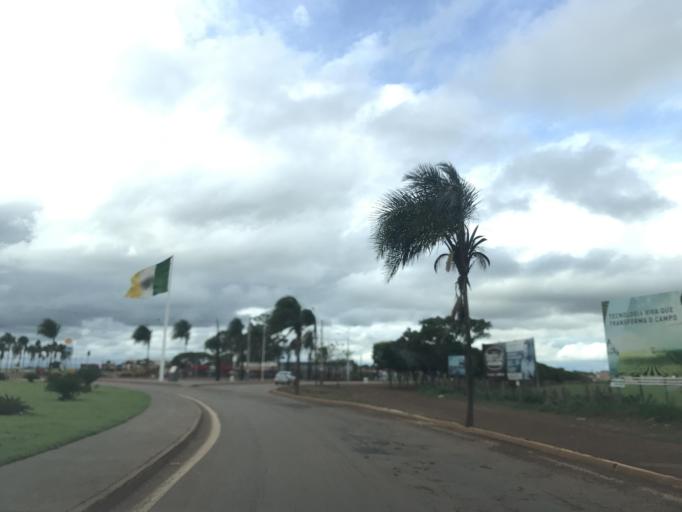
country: BR
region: Goias
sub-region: Vianopolis
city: Vianopolis
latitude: -16.7625
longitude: -48.5209
